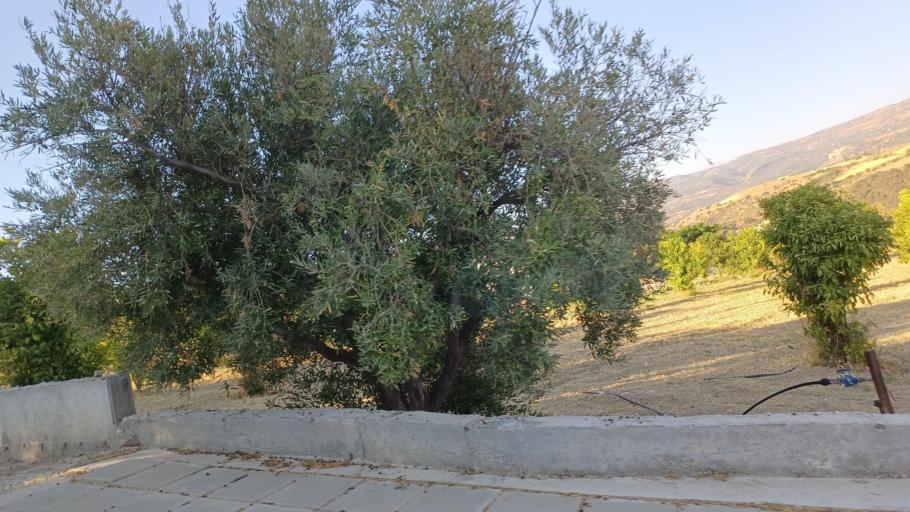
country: CY
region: Pafos
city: Polis
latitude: 34.9958
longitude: 32.4694
